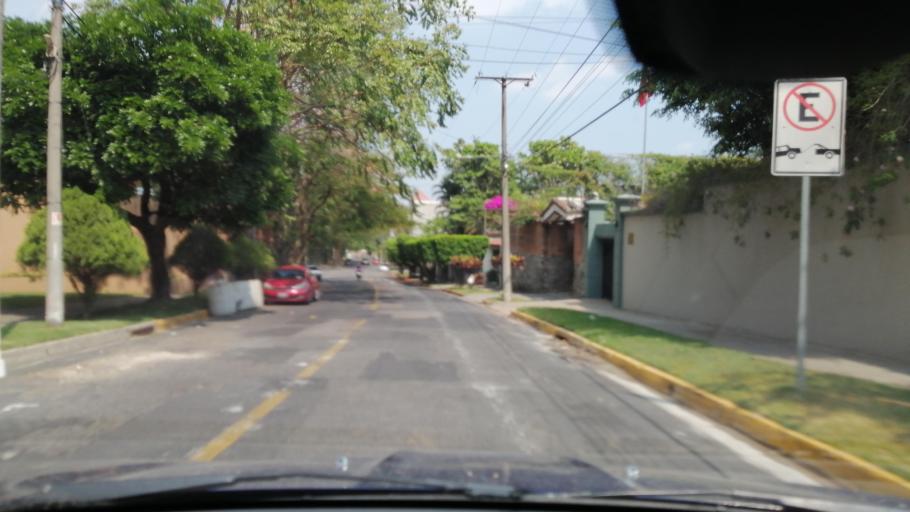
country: SV
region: La Libertad
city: Antiguo Cuscatlan
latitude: 13.6981
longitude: -89.2486
